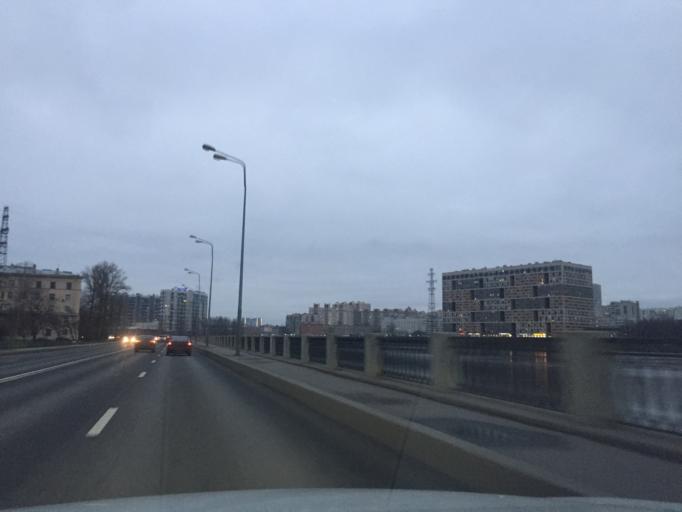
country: RU
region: St.-Petersburg
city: Obukhovo
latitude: 59.8751
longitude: 30.4589
